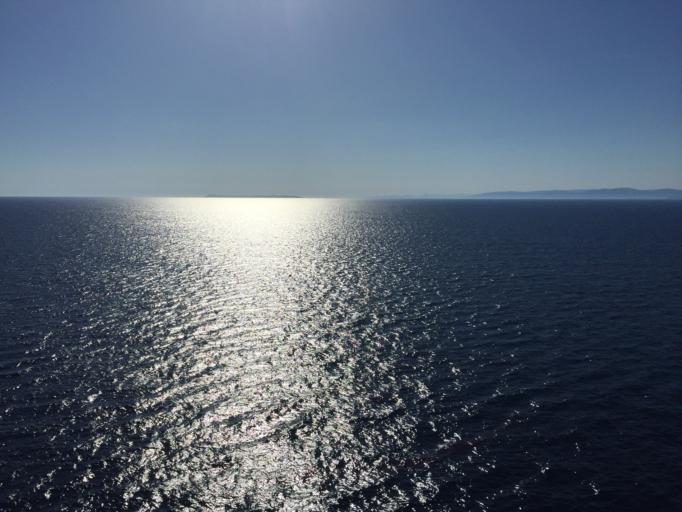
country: FR
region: Provence-Alpes-Cote d'Azur
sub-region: Departement du Var
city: Ramatuelle
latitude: 43.0659
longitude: 6.8454
